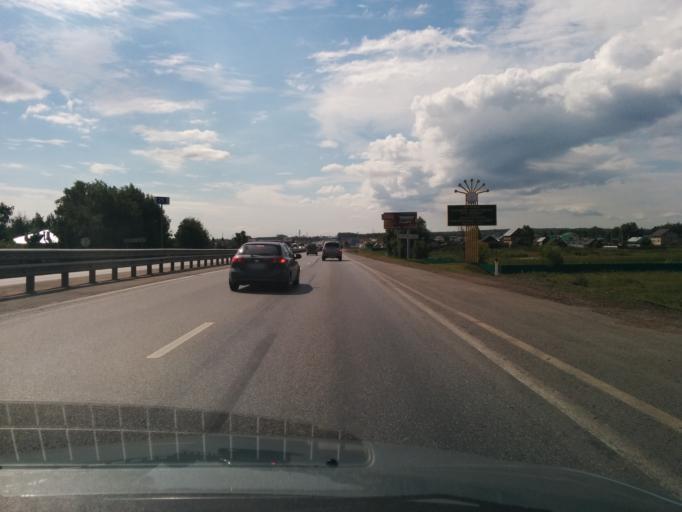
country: RU
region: Bashkortostan
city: Avdon
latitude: 54.5045
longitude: 55.9020
